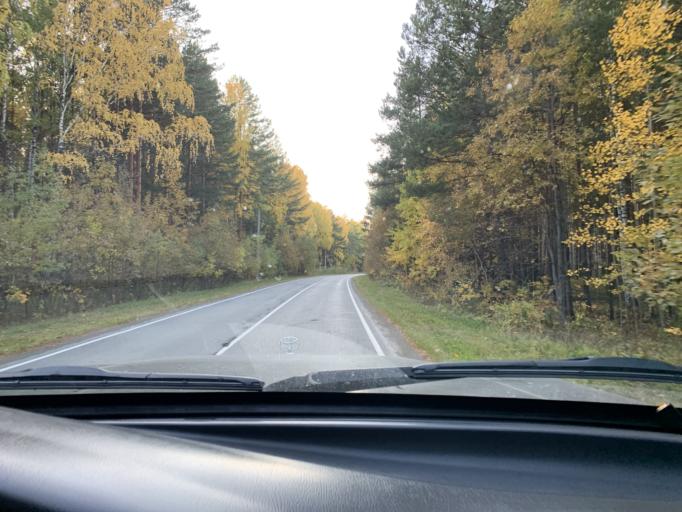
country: RU
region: Sverdlovsk
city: Verkhneye Dubrovo
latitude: 56.8653
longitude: 61.0856
